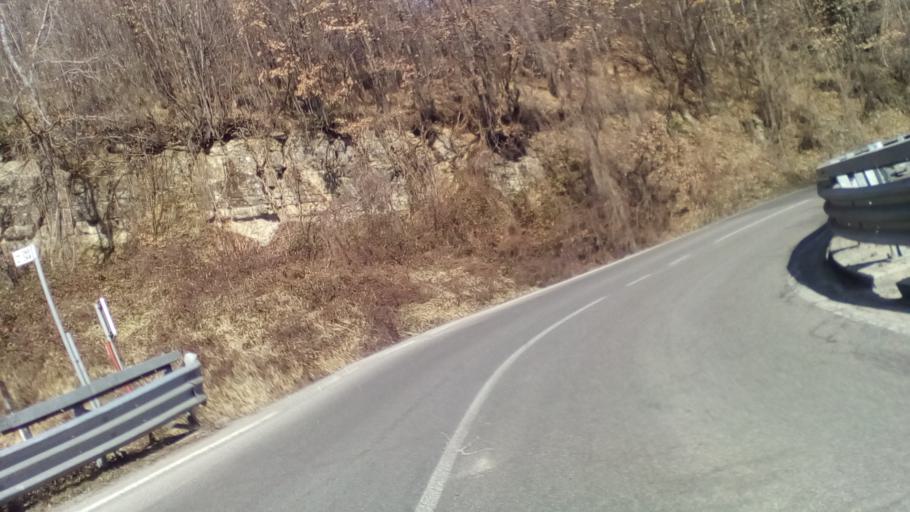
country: IT
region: Emilia-Romagna
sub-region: Provincia di Modena
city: Pavullo nel Frignano
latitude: 44.3099
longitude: 10.8223
